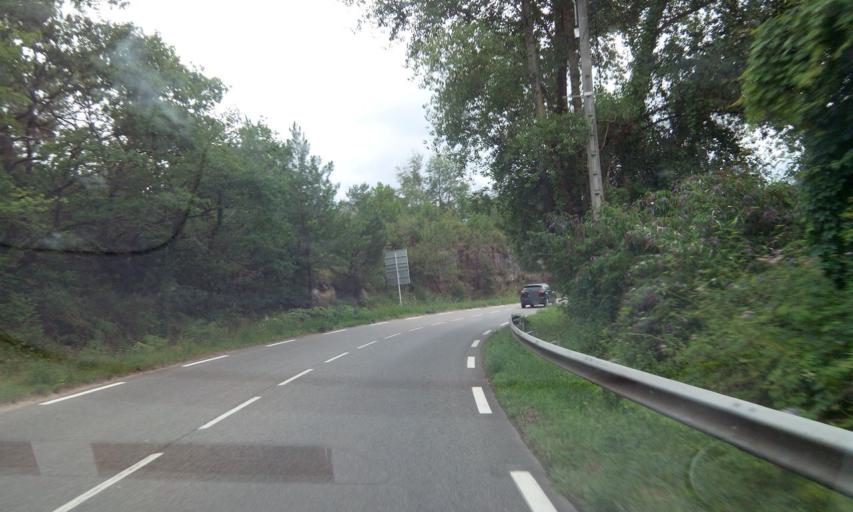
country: FR
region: Limousin
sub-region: Departement de la Correze
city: Cosnac
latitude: 45.1210
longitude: 1.5563
